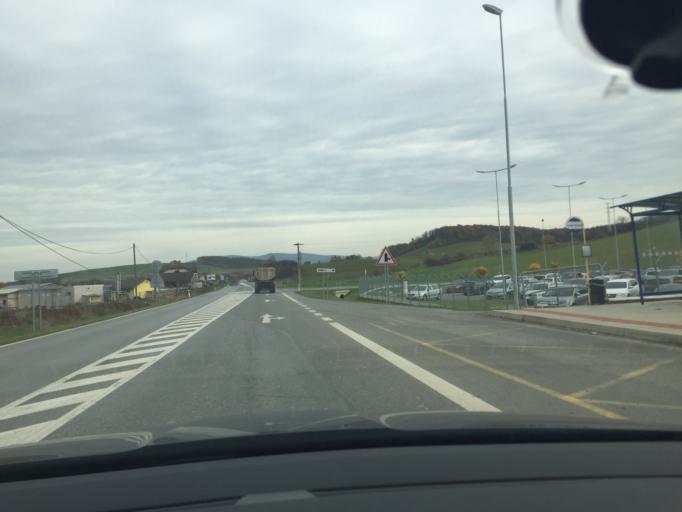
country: SK
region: Presovsky
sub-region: Okres Presov
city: Presov
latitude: 49.0053
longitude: 21.1680
